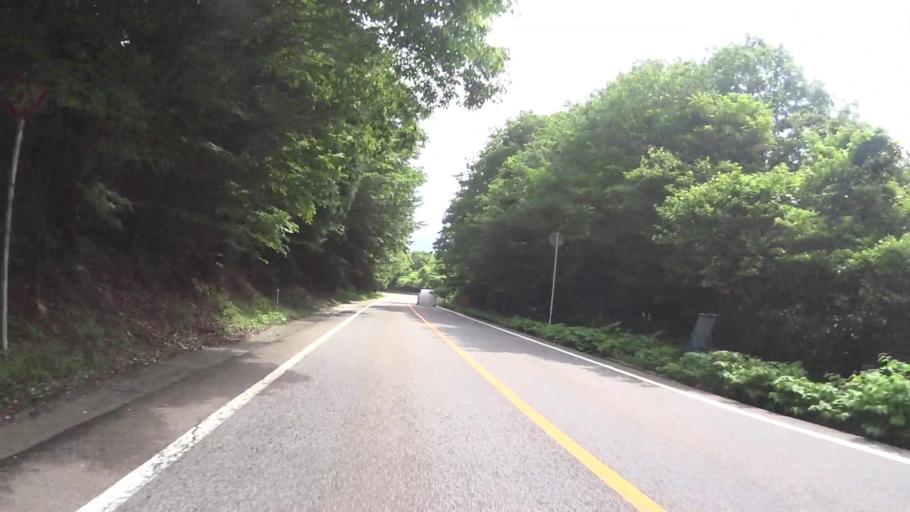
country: JP
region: Kumamoto
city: Aso
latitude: 33.0790
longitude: 131.1965
